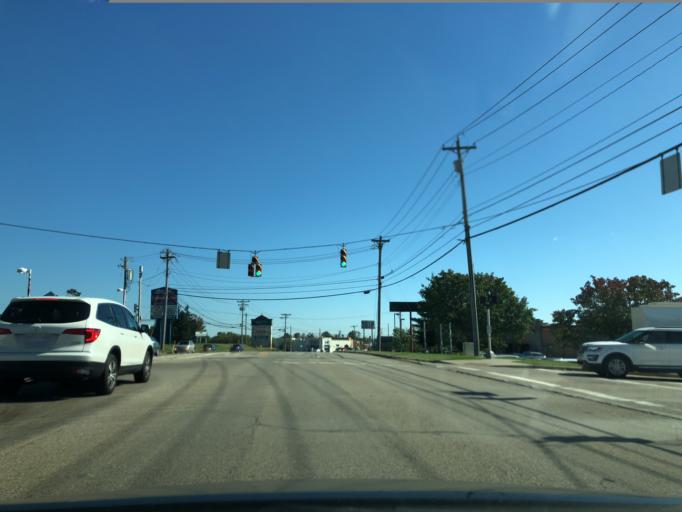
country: US
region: Ohio
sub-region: Hamilton County
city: Sixteen Mile Stand
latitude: 39.2924
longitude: -84.3095
